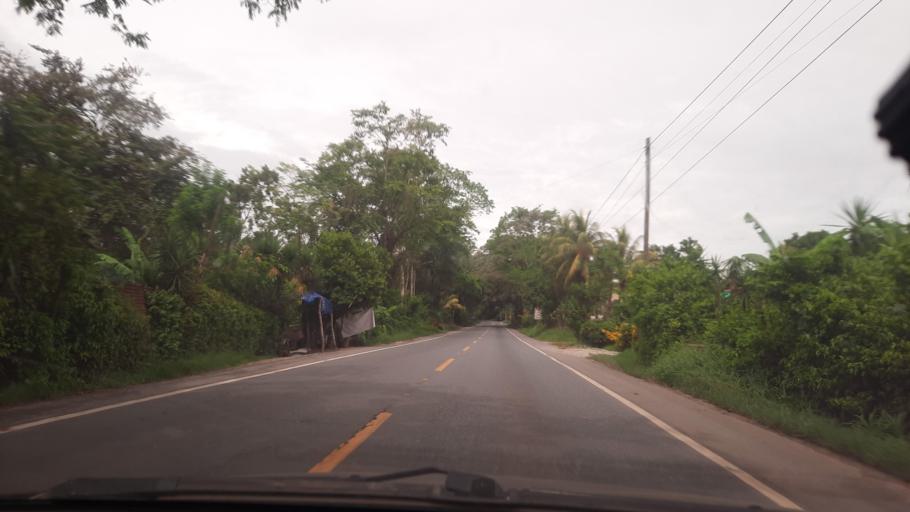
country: GT
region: Izabal
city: Morales
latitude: 15.5122
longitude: -88.8032
